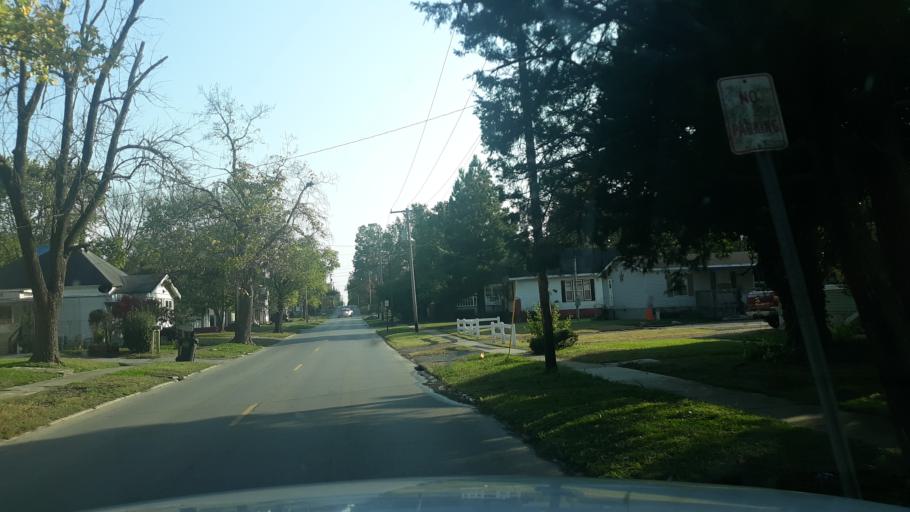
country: US
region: Illinois
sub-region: Saline County
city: Harrisburg
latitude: 37.7301
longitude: -88.5403
